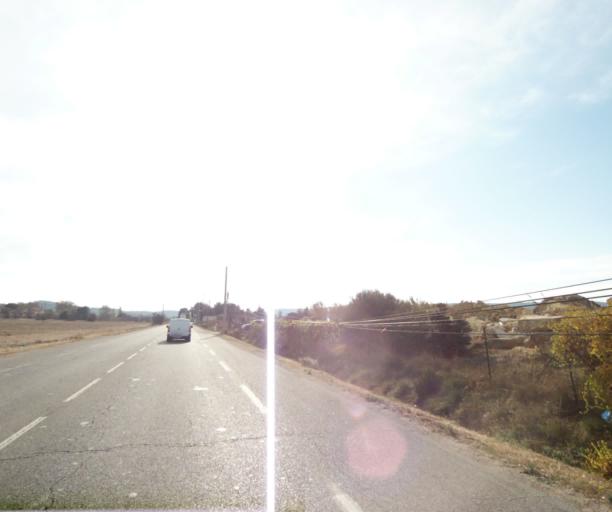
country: FR
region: Provence-Alpes-Cote d'Azur
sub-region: Departement des Bouches-du-Rhone
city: Chateauneuf-les-Martigues
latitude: 43.3903
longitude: 5.1936
